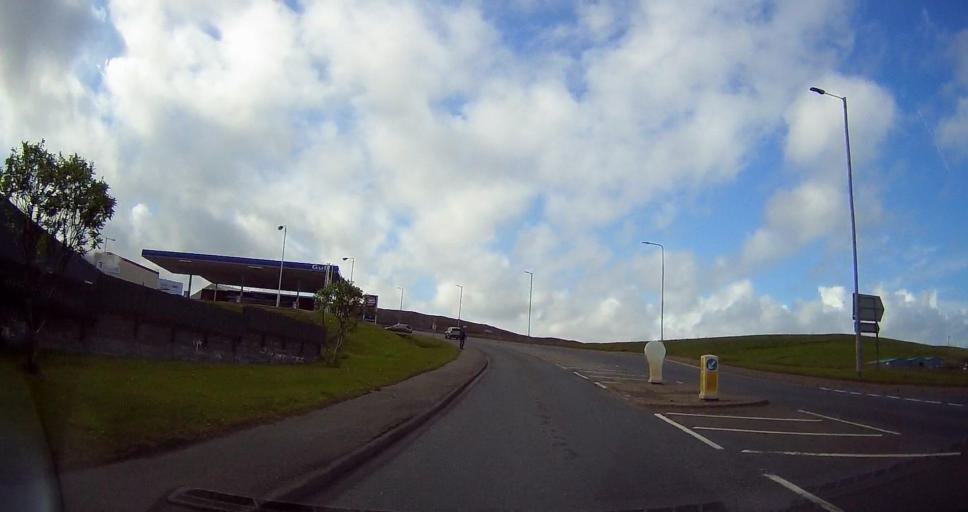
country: GB
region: Scotland
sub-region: Shetland Islands
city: Lerwick
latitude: 60.1687
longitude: -1.1665
